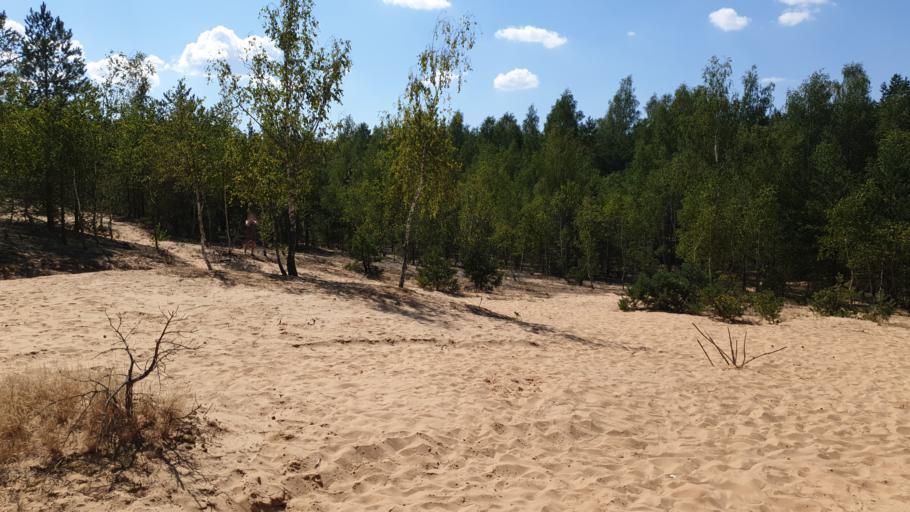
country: LT
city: Sirvintos
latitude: 54.8933
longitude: 24.9535
